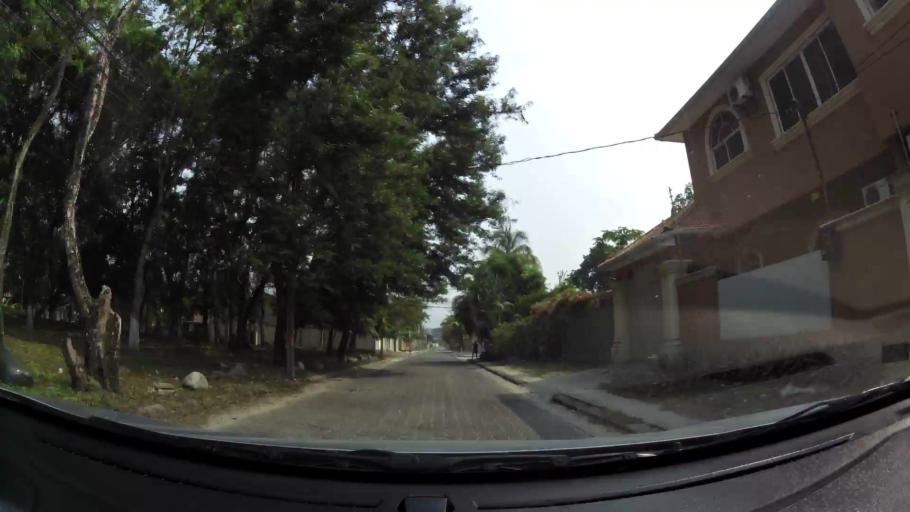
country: HN
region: Cortes
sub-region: San Pedro Sula
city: Pena Blanca
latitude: 15.5322
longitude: -88.0310
